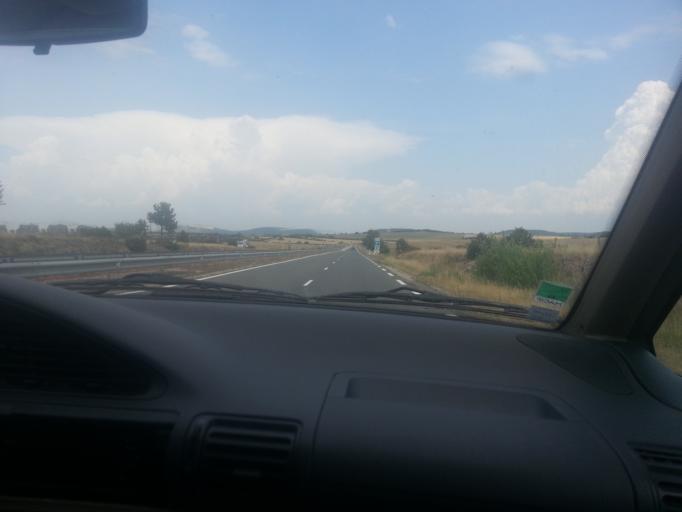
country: FR
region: Midi-Pyrenees
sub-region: Departement de l'Aveyron
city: Millau
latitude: 44.0686
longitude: 3.1145
